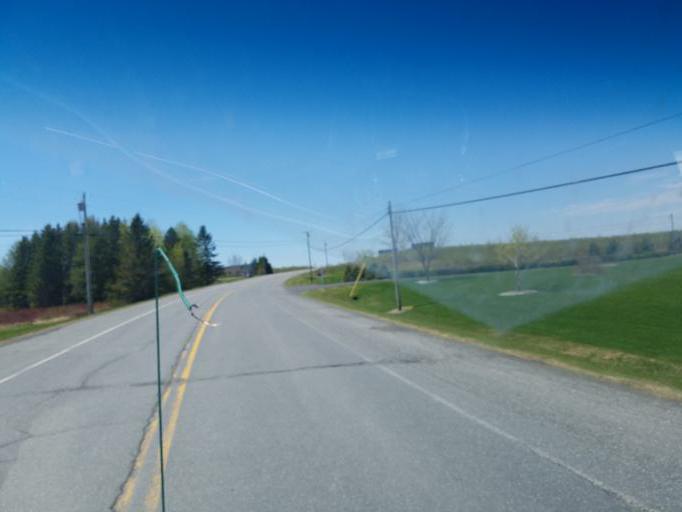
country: US
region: Maine
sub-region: Aroostook County
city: Caribou
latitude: 46.8449
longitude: -68.0509
